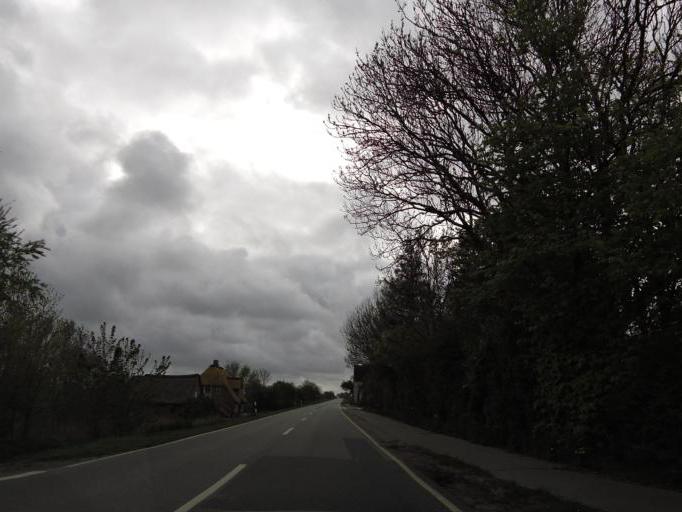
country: DE
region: Schleswig-Holstein
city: Galmsbull
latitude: 54.7749
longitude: 8.7732
